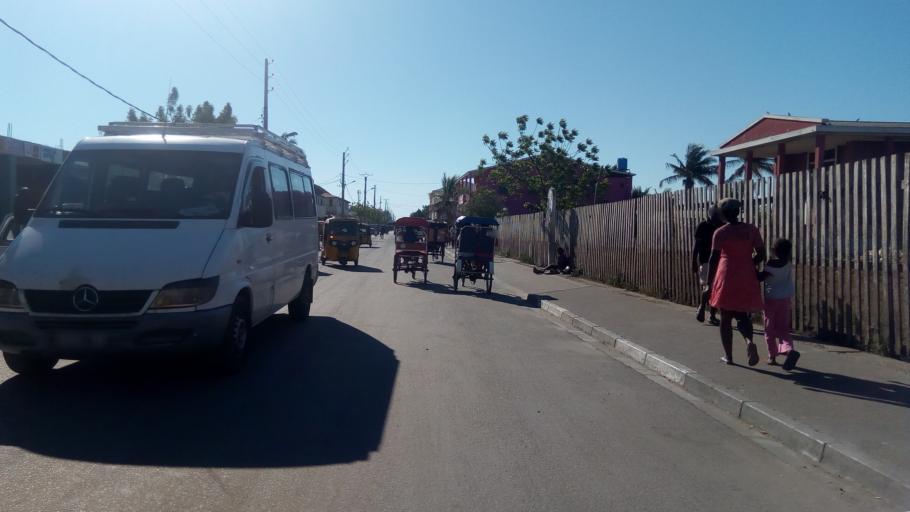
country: MG
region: Menabe
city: Morondava
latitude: -20.2940
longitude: 44.2787
